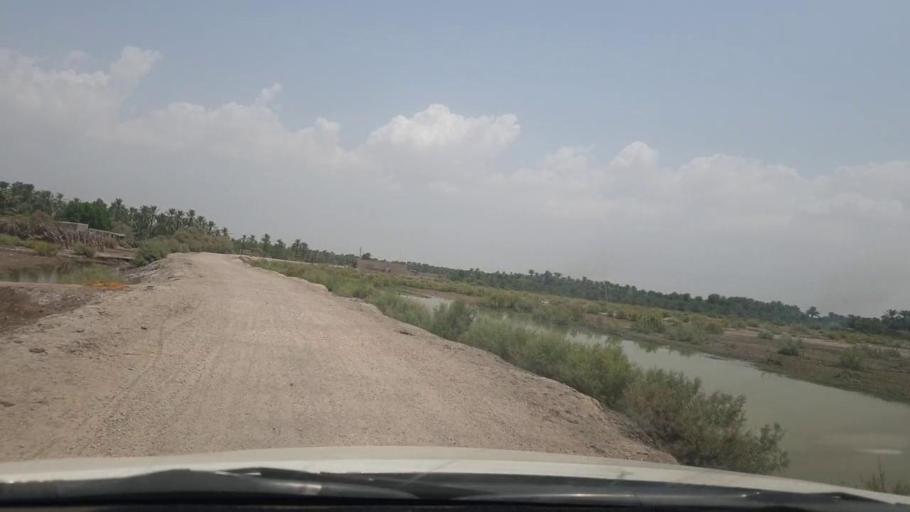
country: PK
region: Sindh
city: Khairpur
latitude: 27.5491
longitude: 68.8193
